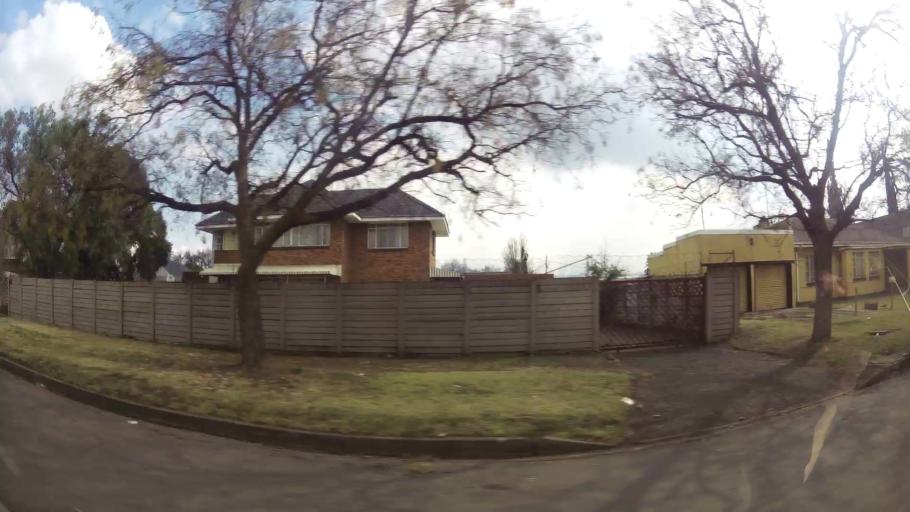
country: ZA
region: Gauteng
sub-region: Sedibeng District Municipality
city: Vereeniging
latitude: -26.6786
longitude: 27.9241
